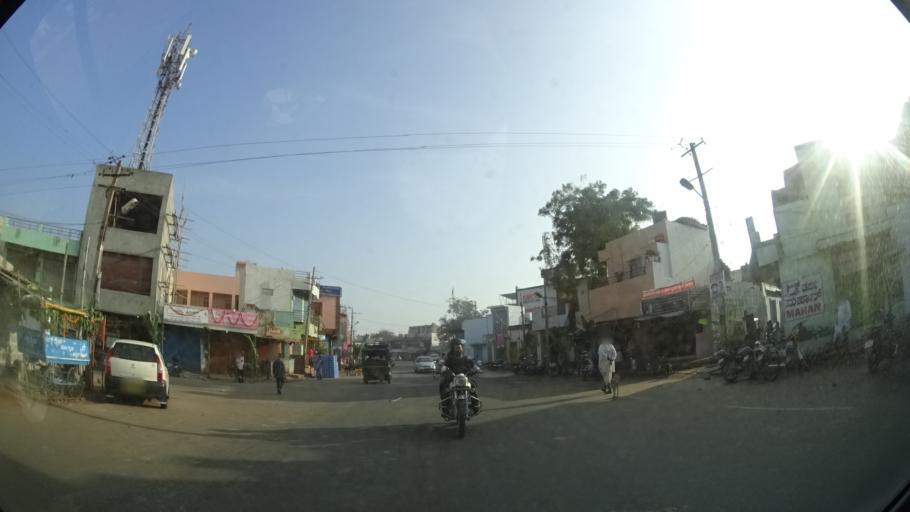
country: IN
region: Karnataka
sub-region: Bellary
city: Hospet
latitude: 15.2700
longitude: 76.3895
